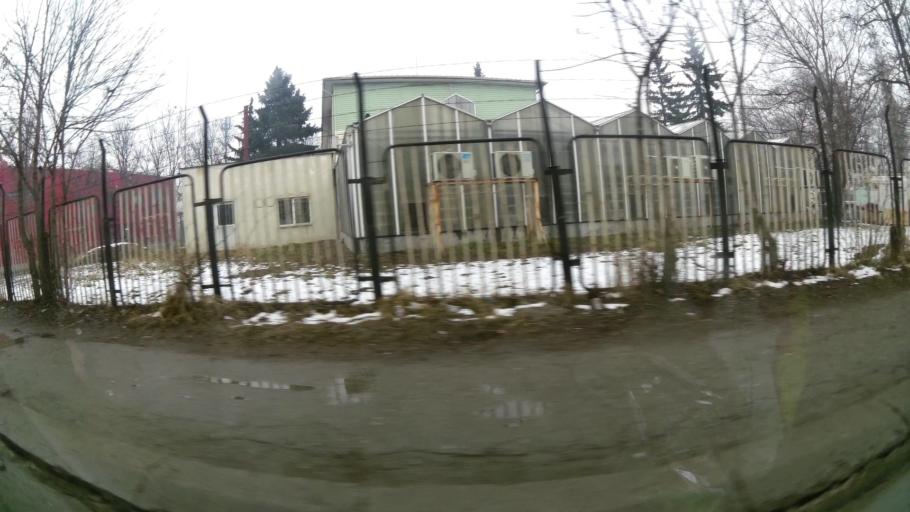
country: BG
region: Sofia-Capital
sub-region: Stolichna Obshtina
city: Sofia
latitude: 42.6868
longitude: 23.2734
